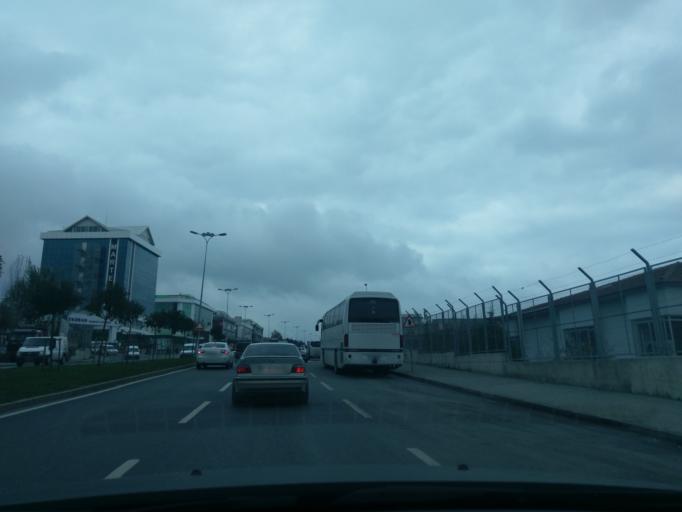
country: TR
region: Istanbul
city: Basaksehir
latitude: 41.0732
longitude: 28.8015
